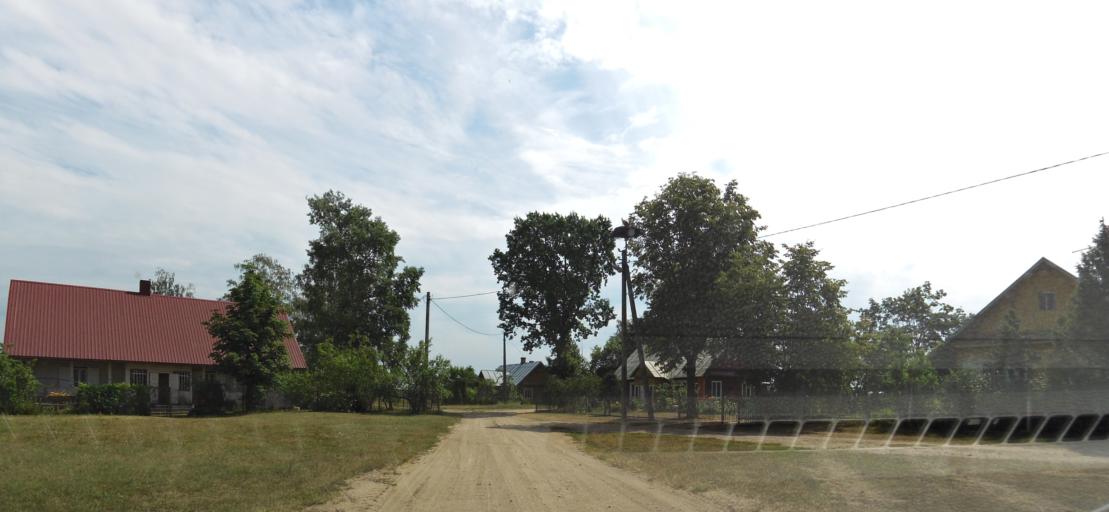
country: LT
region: Vilnius County
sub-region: Trakai
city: Rudiskes
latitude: 54.3696
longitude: 24.8543
